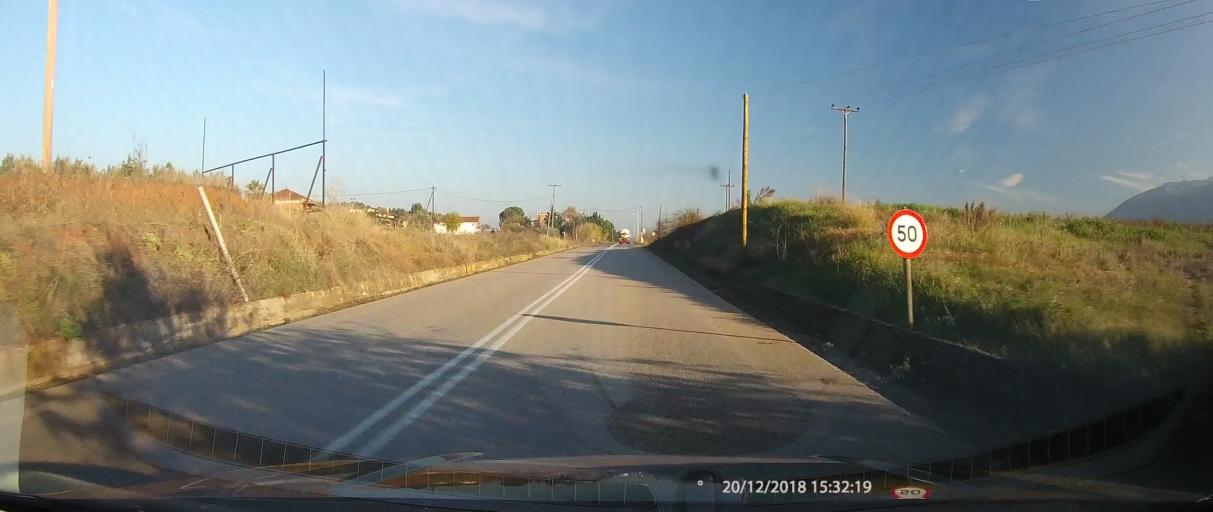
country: GR
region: Central Greece
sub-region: Nomos Fthiotidos
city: Lianokladhion
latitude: 38.9292
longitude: 22.2564
